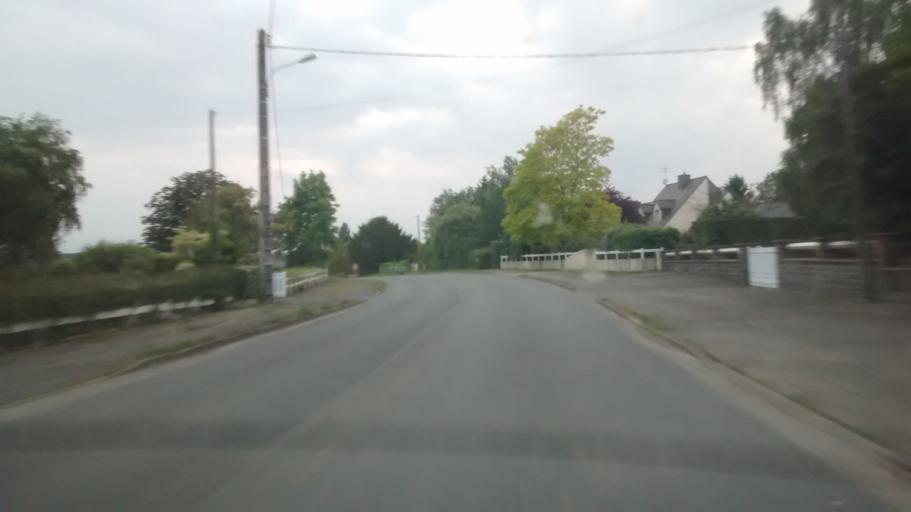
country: FR
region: Brittany
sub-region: Departement du Morbihan
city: Saint-Martin-sur-Oust
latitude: 47.7453
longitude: -2.2461
